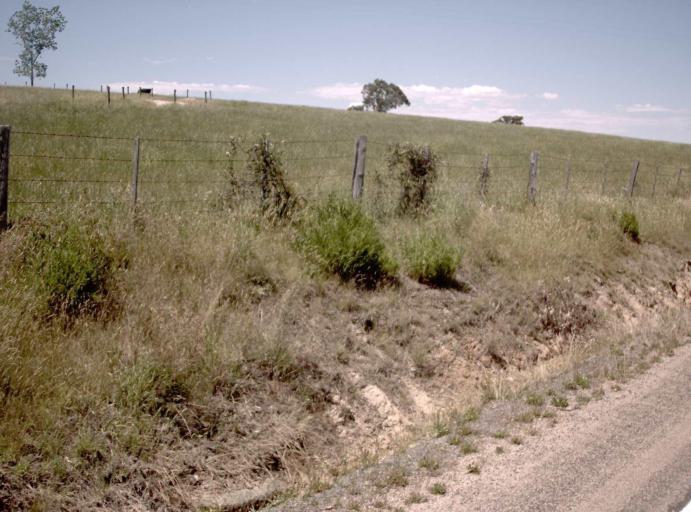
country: AU
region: Victoria
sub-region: East Gippsland
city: Lakes Entrance
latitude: -37.7059
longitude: 148.4983
